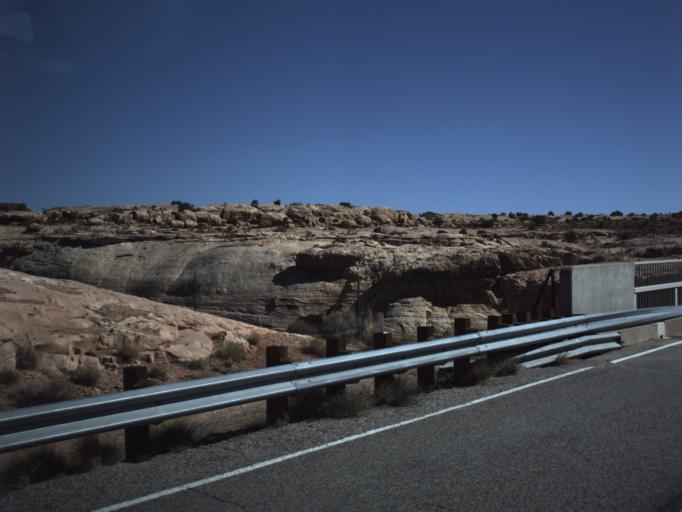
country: US
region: Utah
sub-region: San Juan County
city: Blanding
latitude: 37.8202
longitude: -110.3517
